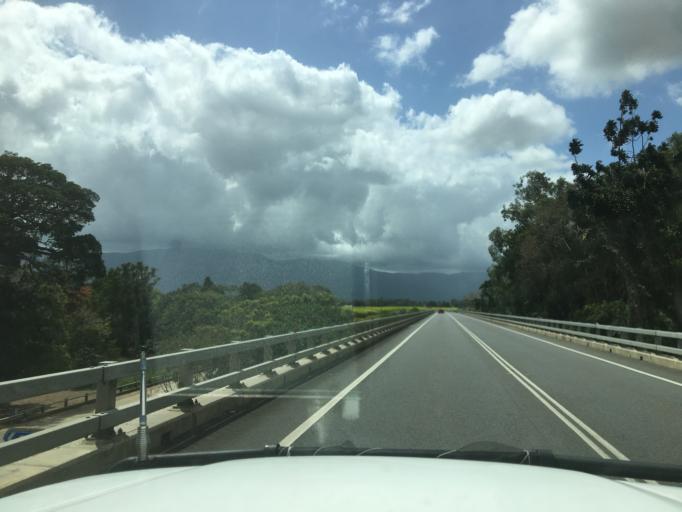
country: AU
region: Queensland
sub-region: Cairns
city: Woree
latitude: -17.1010
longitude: 145.7868
